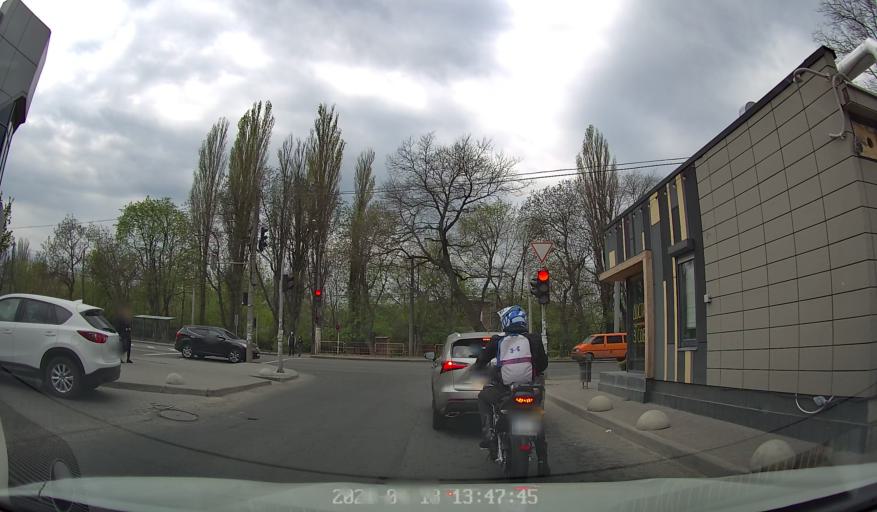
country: GR
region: South Aegean
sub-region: Nomos Kykladon
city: Serifos
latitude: 37.1374
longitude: 24.5806
